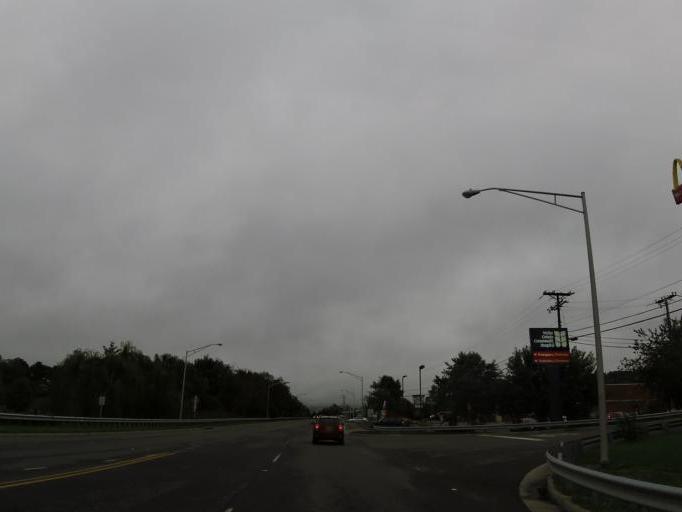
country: US
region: Virginia
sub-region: Wythe County
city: Wytheville
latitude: 36.9580
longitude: -81.0954
